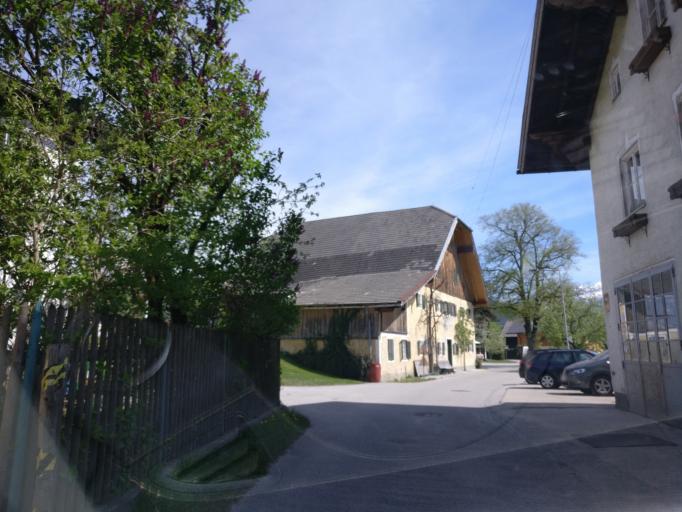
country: AT
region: Salzburg
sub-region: Politischer Bezirk Hallein
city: Kuchl
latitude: 47.6376
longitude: 13.1477
